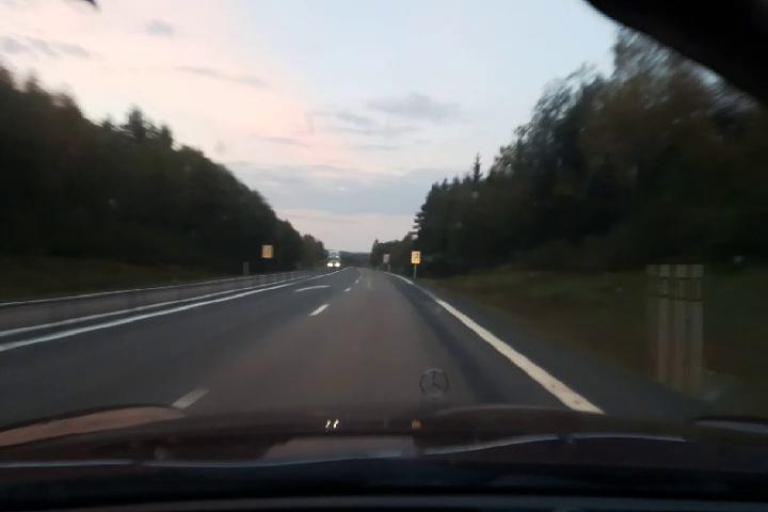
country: SE
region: Vaesternorrland
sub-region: Haernoesands Kommun
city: Haernoesand
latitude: 62.8684
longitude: 18.0395
